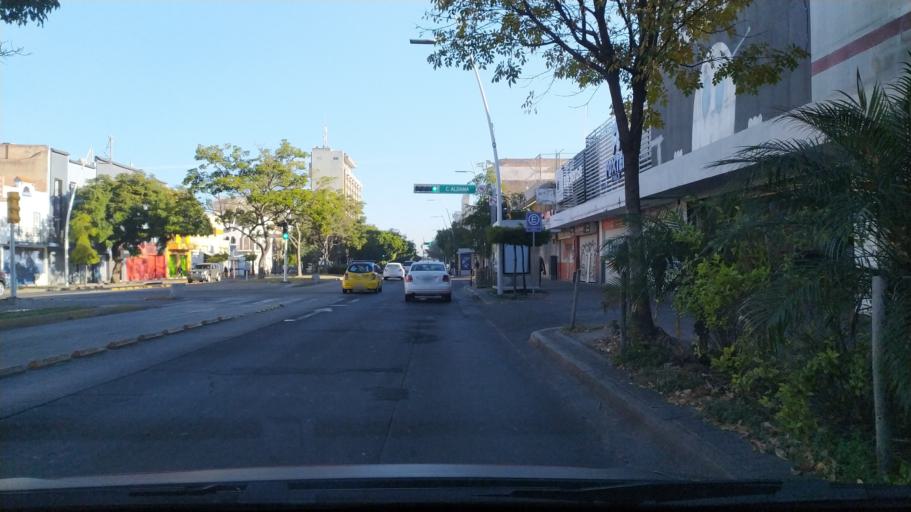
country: MX
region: Jalisco
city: Guadalajara
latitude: 20.6721
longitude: -103.3434
